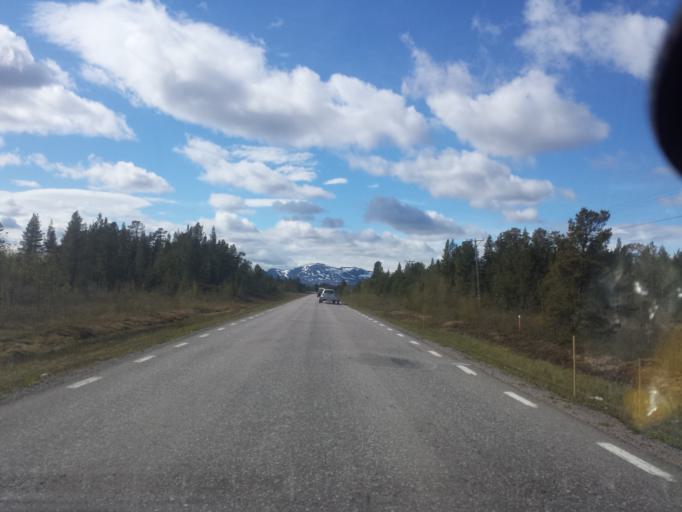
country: SE
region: Norrbotten
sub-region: Kiruna Kommun
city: Kiruna
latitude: 67.9914
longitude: 19.9195
